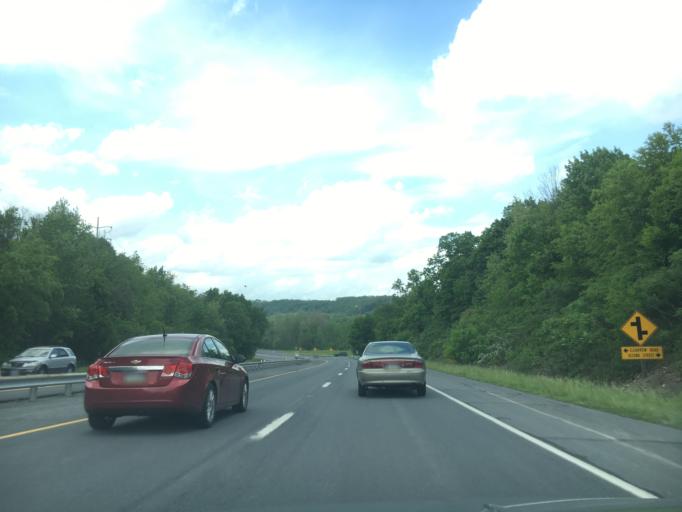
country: US
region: Pennsylvania
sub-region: Lehigh County
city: Cementon
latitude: 40.7039
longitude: -75.5209
